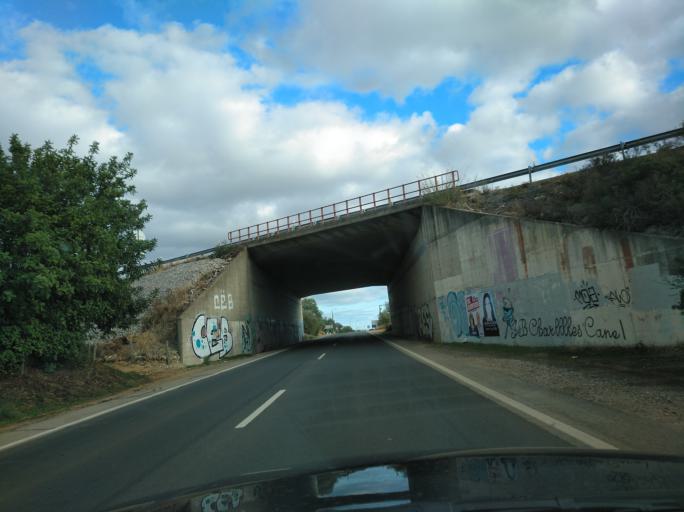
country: PT
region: Faro
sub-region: Tavira
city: Luz
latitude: 37.1363
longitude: -7.6990
